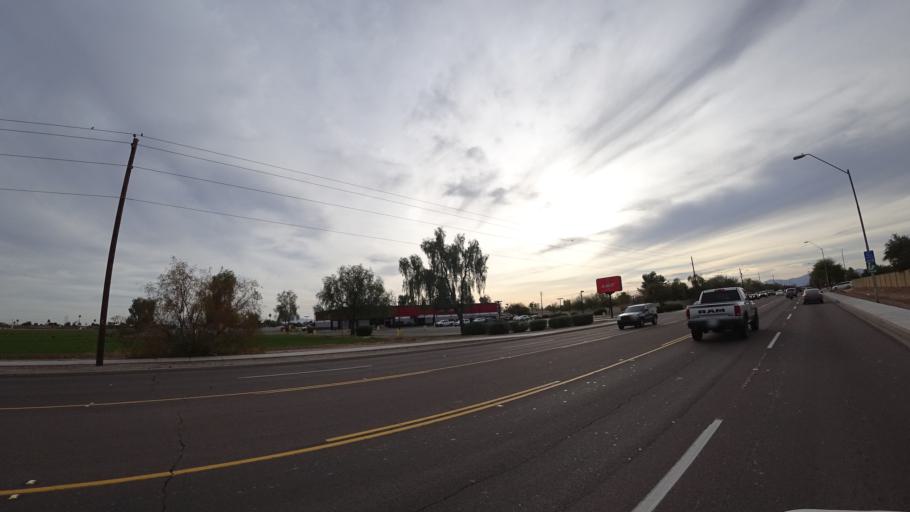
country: US
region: Arizona
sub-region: Maricopa County
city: Peoria
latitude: 33.5664
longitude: -112.2410
